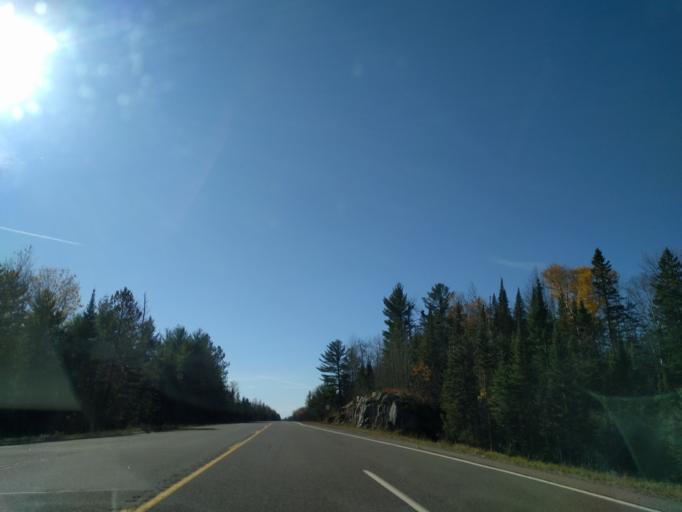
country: US
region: Michigan
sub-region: Marquette County
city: West Ishpeming
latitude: 46.4258
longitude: -87.9749
